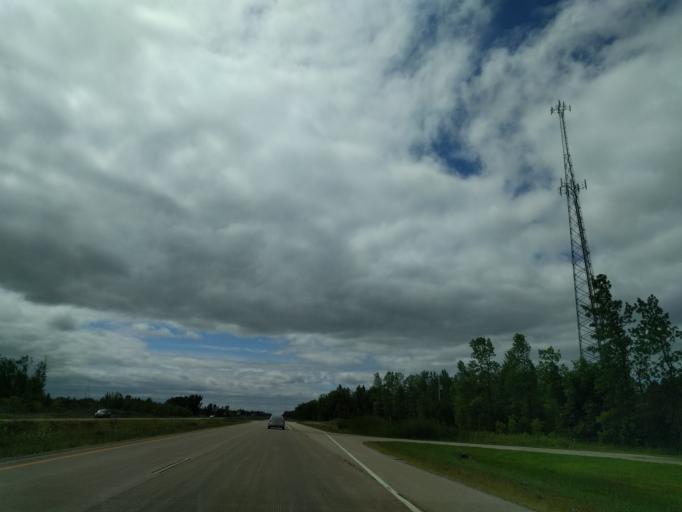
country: US
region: Wisconsin
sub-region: Oconto County
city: Oconto
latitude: 44.9989
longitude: -87.8532
